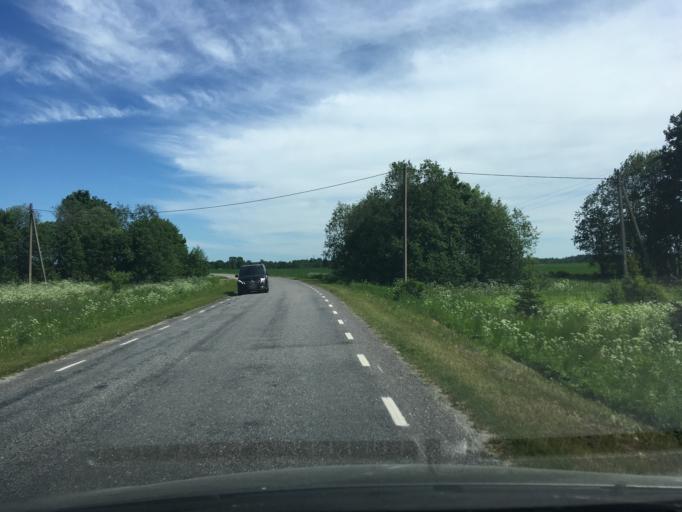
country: EE
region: Raplamaa
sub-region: Rapla vald
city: Rapla
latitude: 59.0441
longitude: 24.8675
